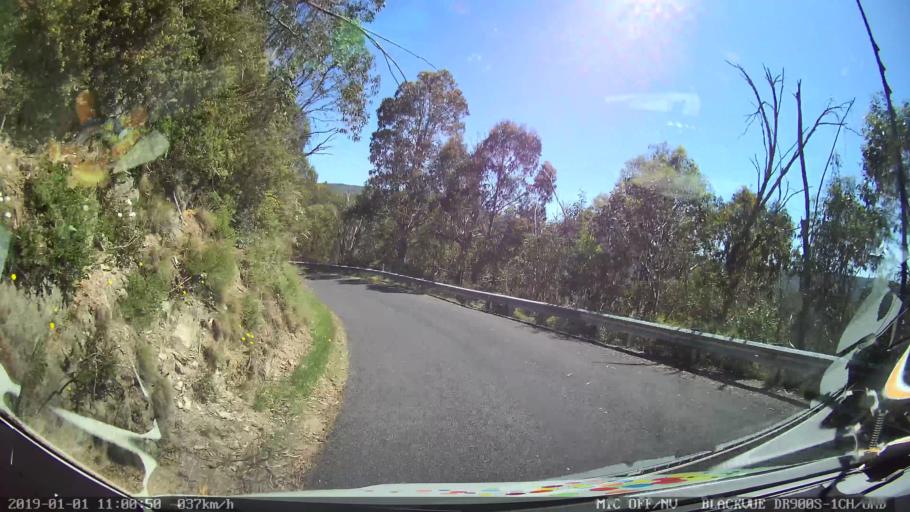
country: AU
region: New South Wales
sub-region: Snowy River
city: Jindabyne
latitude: -35.9798
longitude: 148.3981
